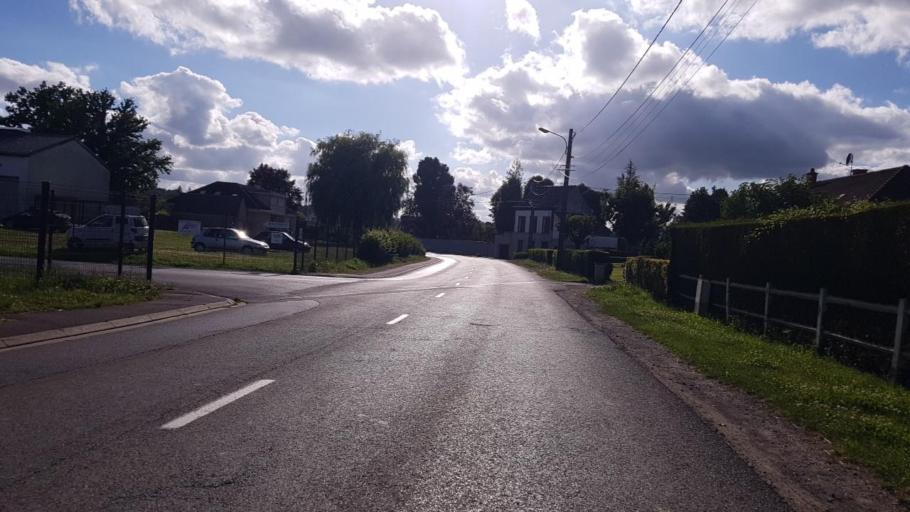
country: FR
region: Picardie
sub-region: Departement de l'Aisne
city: Hirson
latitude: 49.9219
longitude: 4.0673
